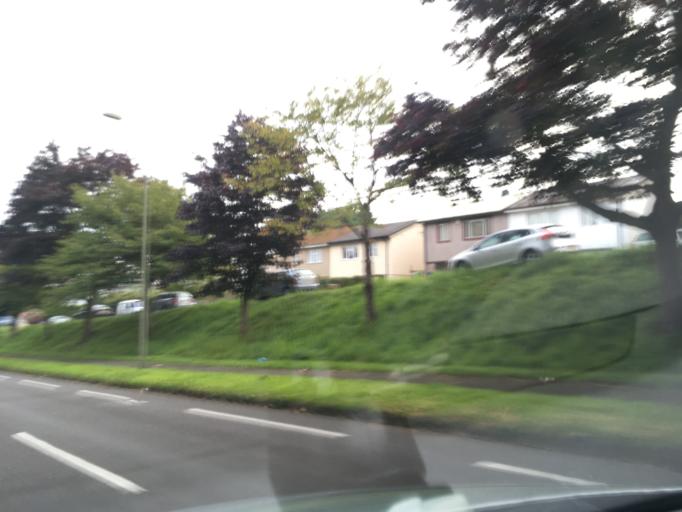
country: GB
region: England
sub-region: Oxfordshire
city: Cowley
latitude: 51.7655
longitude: -1.1930
